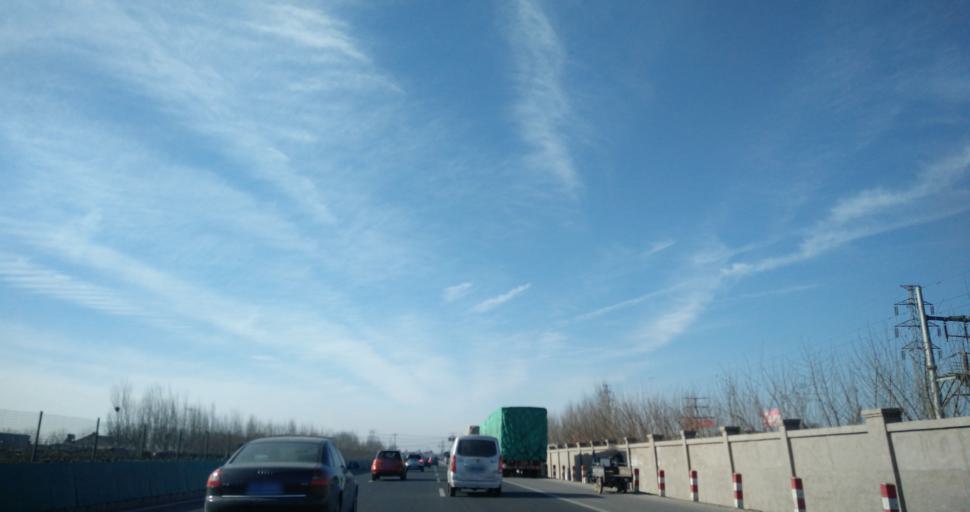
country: CN
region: Beijing
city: Yinghai
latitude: 39.7422
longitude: 116.3898
